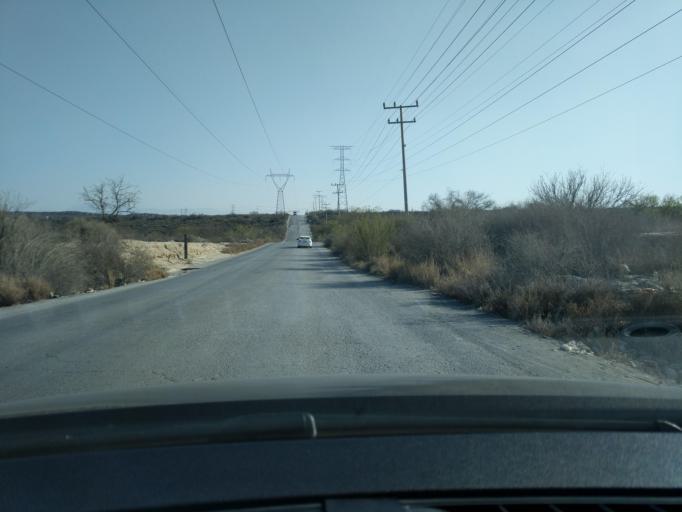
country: MX
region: Coahuila
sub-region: Ramos Arizpe
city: Ramos Arizpe
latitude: 25.5384
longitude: -100.9780
